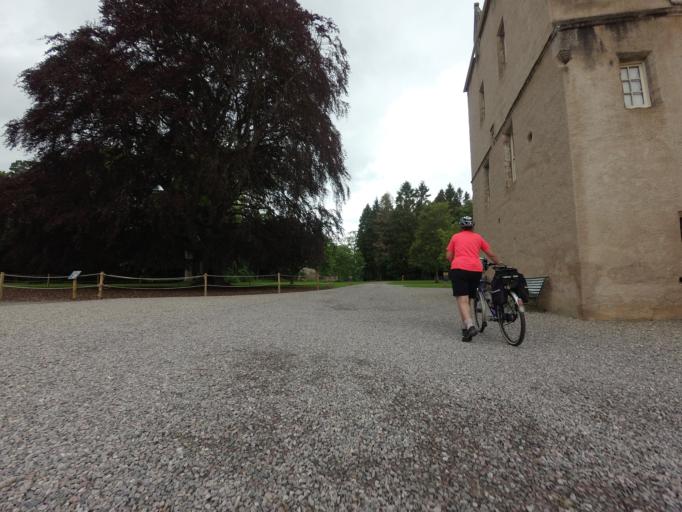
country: GB
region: Scotland
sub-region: Moray
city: Forres
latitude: 57.5981
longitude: -3.7090
